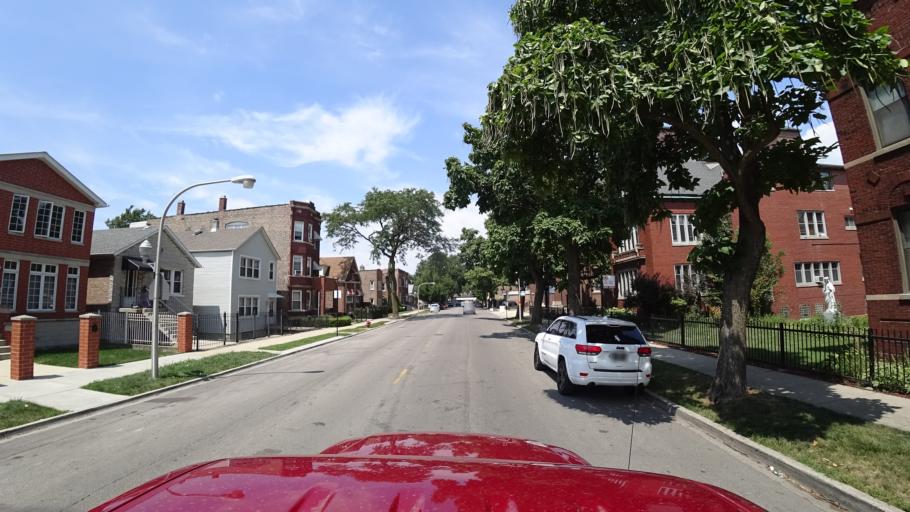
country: US
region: Illinois
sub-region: Cook County
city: Chicago
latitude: 41.8419
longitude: -87.6527
